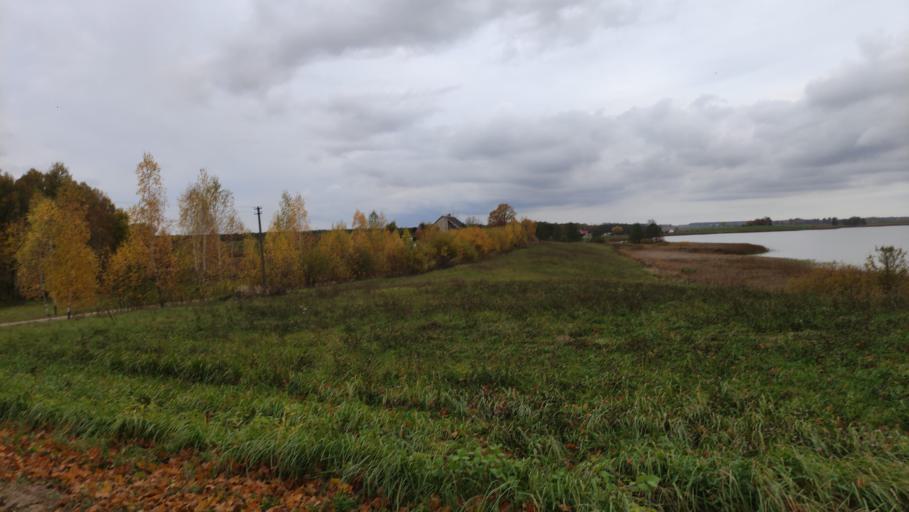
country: LT
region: Alytaus apskritis
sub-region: Alytus
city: Alytus
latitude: 54.4315
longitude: 23.8579
